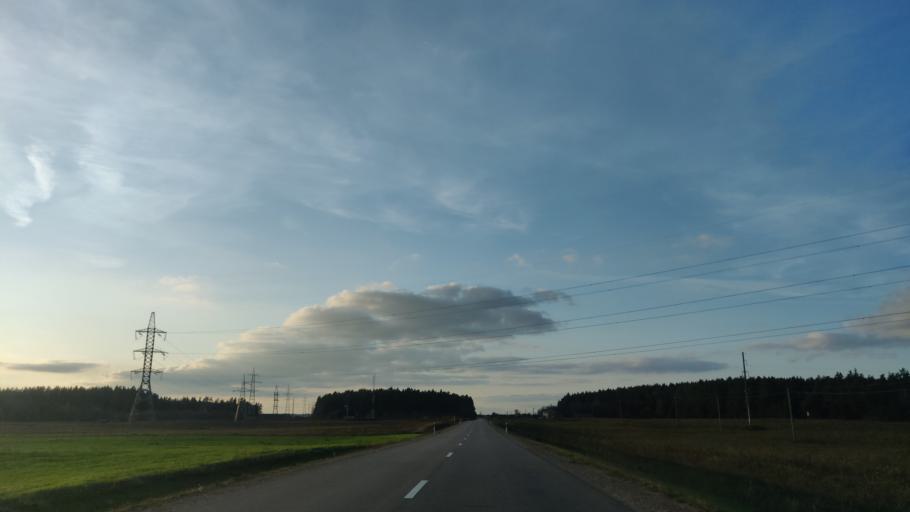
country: LT
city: Lentvaris
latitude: 54.5958
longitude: 25.0355
